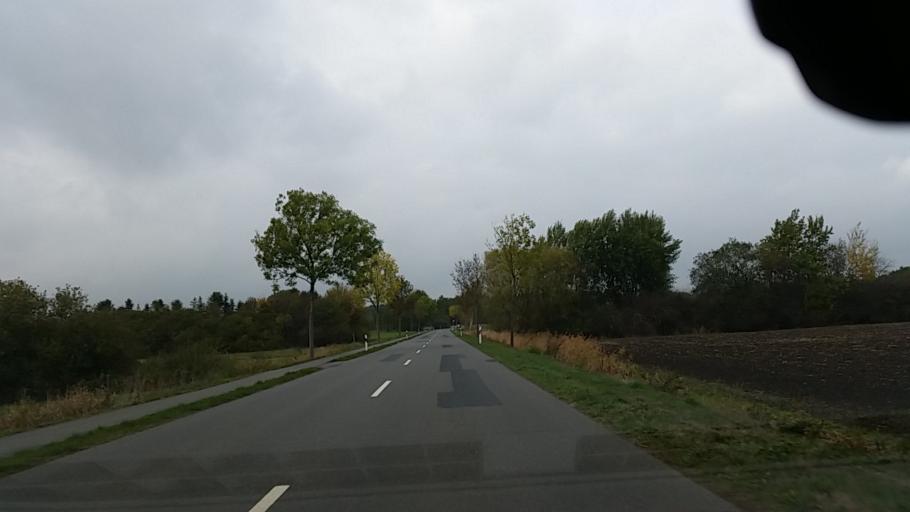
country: DE
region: Lower Saxony
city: Jembke
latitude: 52.4886
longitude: 10.7655
